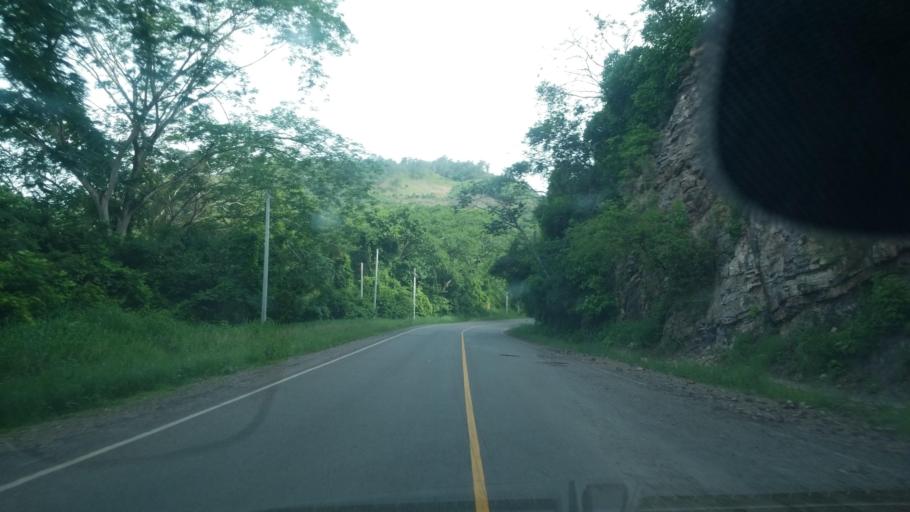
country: HN
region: Santa Barbara
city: Ilama
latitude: 15.0929
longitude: -88.2056
